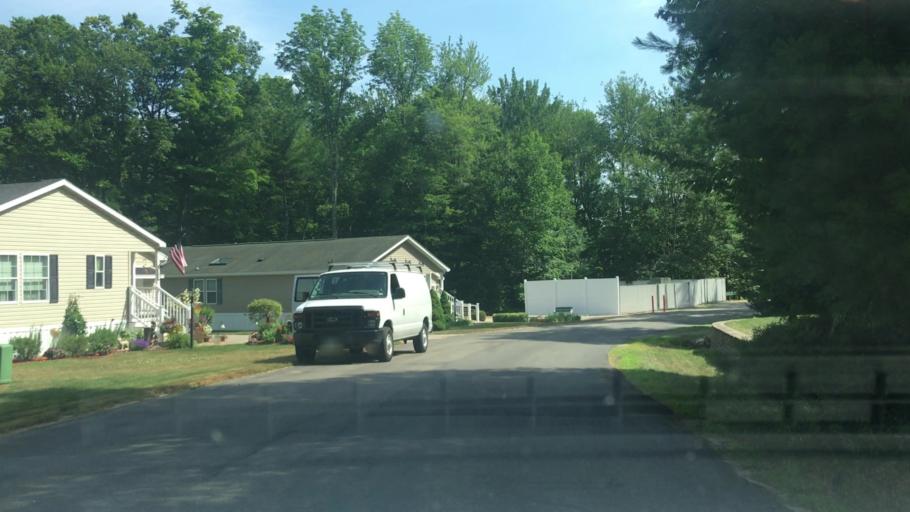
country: US
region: New Hampshire
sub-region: Strafford County
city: Rochester
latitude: 43.3149
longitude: -70.9236
